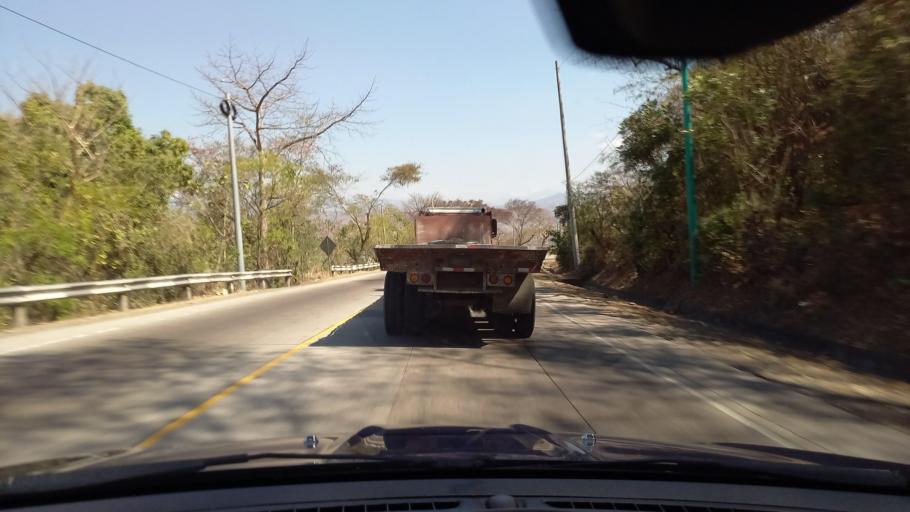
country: SV
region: Santa Ana
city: Santa Ana
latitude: 14.0550
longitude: -89.5151
